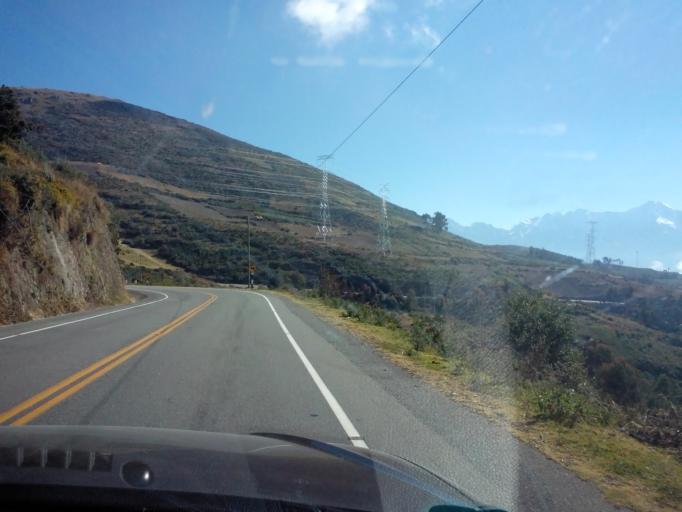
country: PE
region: Apurimac
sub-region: Provincia de Abancay
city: Cachora
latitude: -13.5501
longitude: -72.8086
